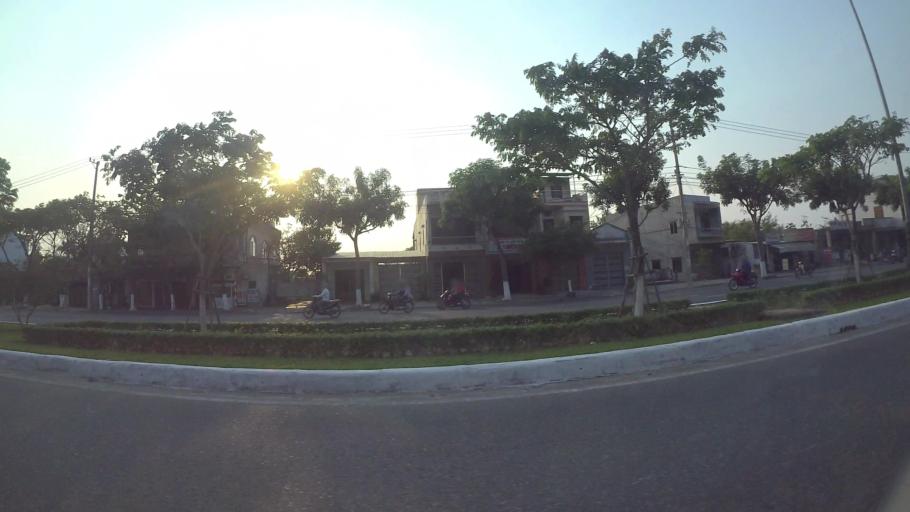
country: VN
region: Da Nang
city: Ngu Hanh Son
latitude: 15.9843
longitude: 108.2564
